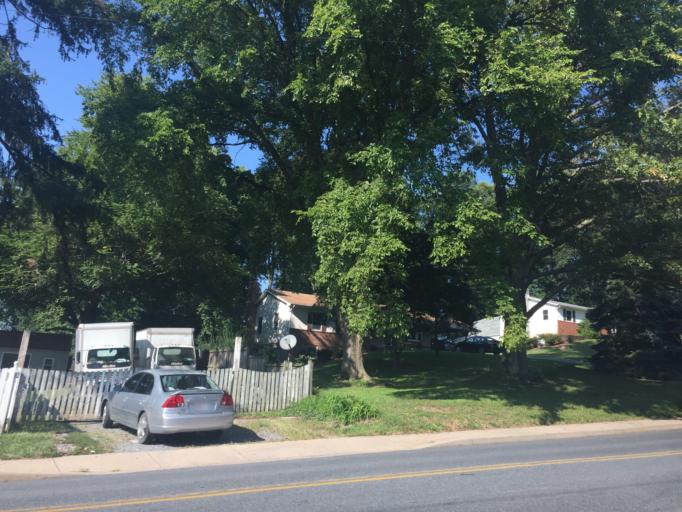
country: US
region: Maryland
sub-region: Carroll County
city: Mount Airy
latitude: 39.3795
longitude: -77.1634
